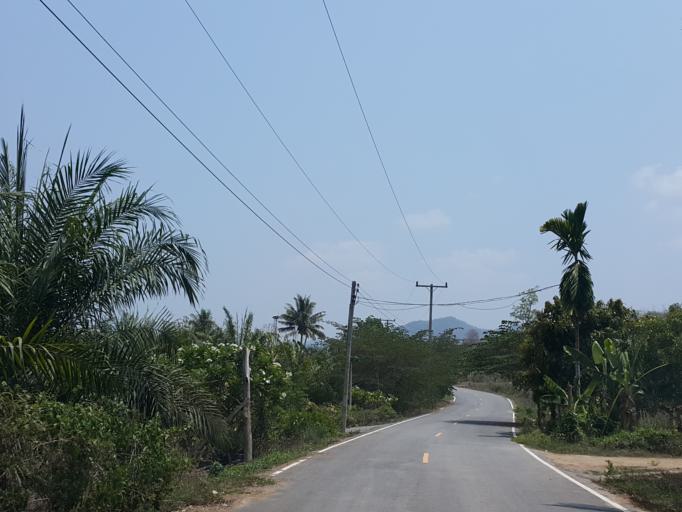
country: TH
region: Kanchanaburi
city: Sai Yok
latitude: 14.1813
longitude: 98.9557
